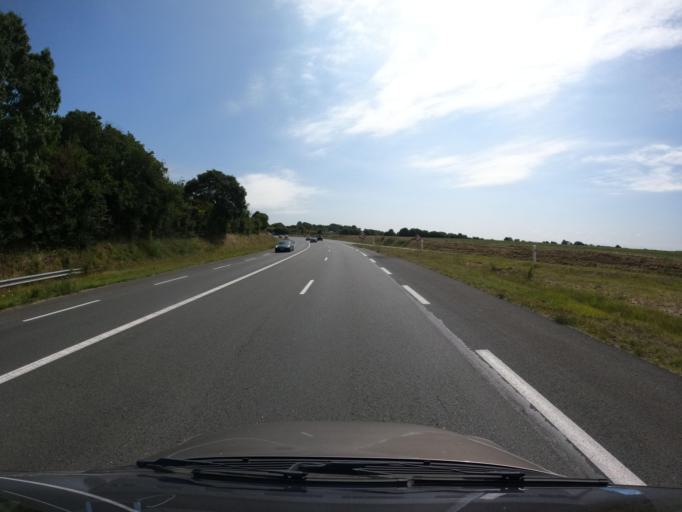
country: FR
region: Poitou-Charentes
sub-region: Departement des Deux-Sevres
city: Mauze-sur-le-Mignon
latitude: 46.1883
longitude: -0.6778
